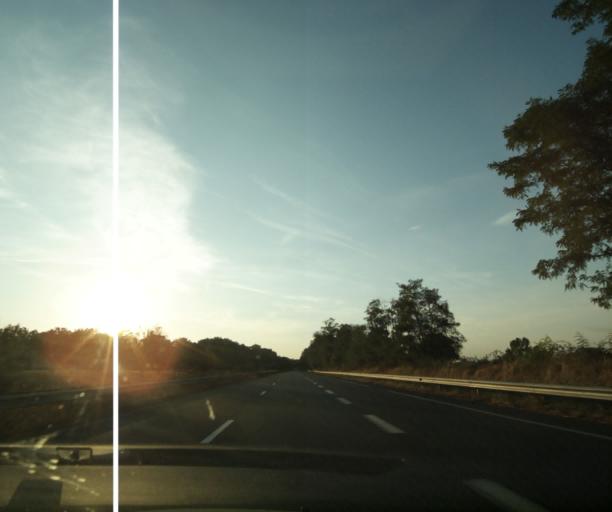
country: FR
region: Aquitaine
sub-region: Departement du Lot-et-Garonne
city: Layrac
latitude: 44.1263
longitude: 0.6956
